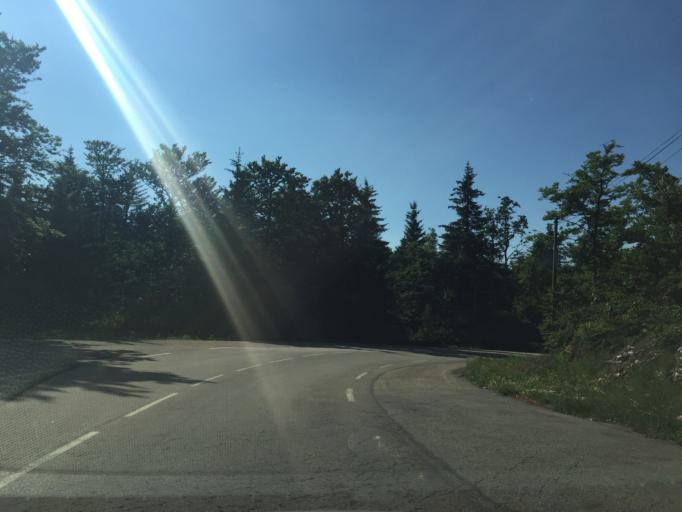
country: FR
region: Rhone-Alpes
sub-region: Departement de la Drome
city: Saint-Jean-en-Royans
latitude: 44.9087
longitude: 5.3331
